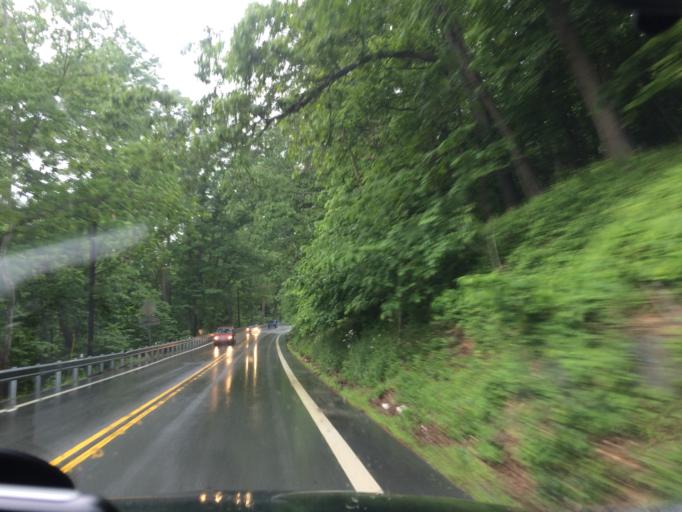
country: US
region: Maryland
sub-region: Frederick County
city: Thurmont
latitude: 39.6589
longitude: -77.4449
